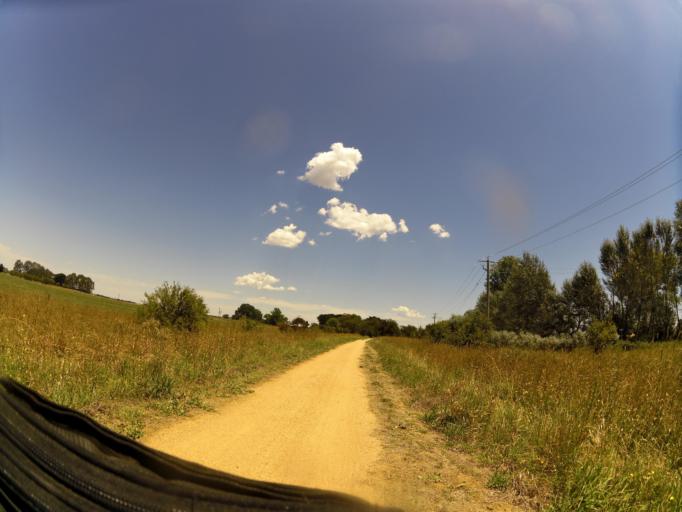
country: AU
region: Victoria
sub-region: Wellington
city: Heyfield
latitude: -37.9668
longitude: 146.9129
